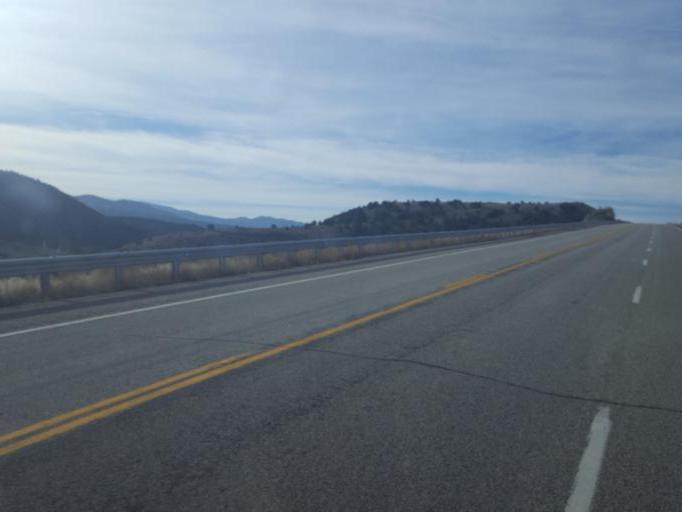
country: US
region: Colorado
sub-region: Costilla County
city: San Luis
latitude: 37.4915
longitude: -105.3401
